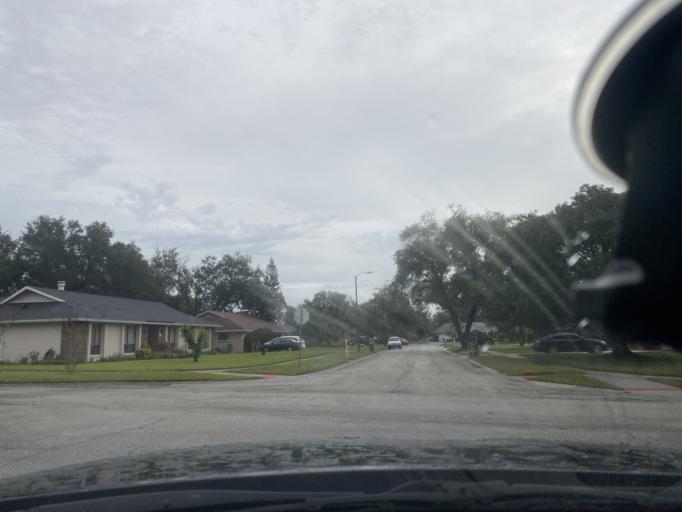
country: US
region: Florida
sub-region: Orange County
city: Union Park
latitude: 28.5385
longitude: -81.2627
